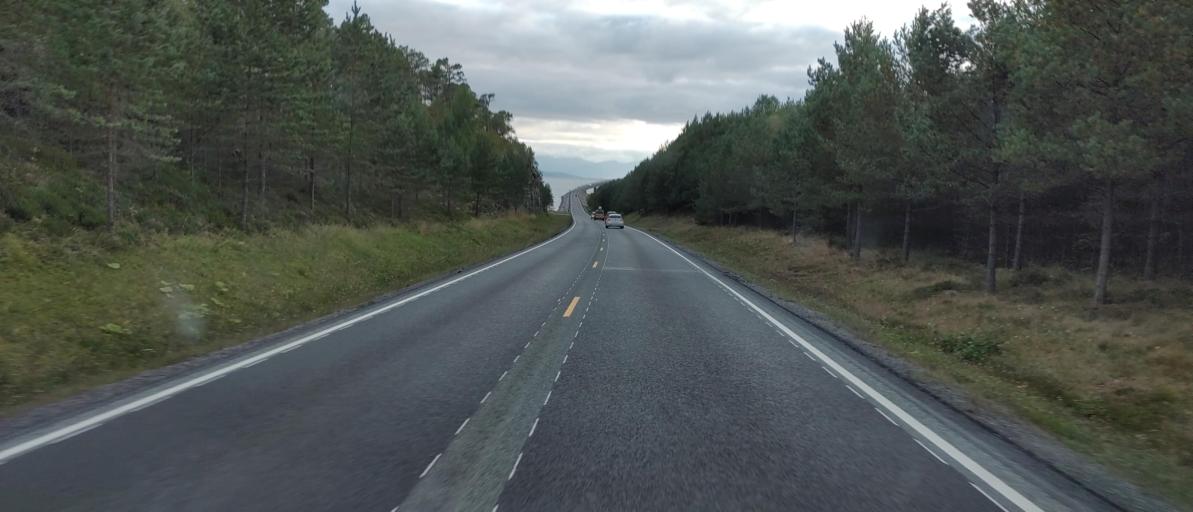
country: NO
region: More og Romsdal
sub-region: Molde
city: Hjelset
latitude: 62.7339
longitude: 7.3772
